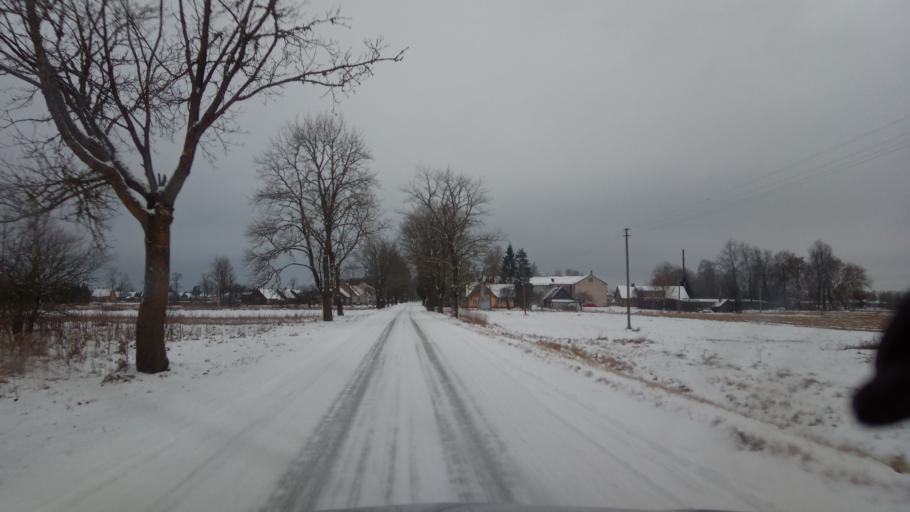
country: LT
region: Vilnius County
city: Ukmerge
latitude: 55.4970
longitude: 24.6124
